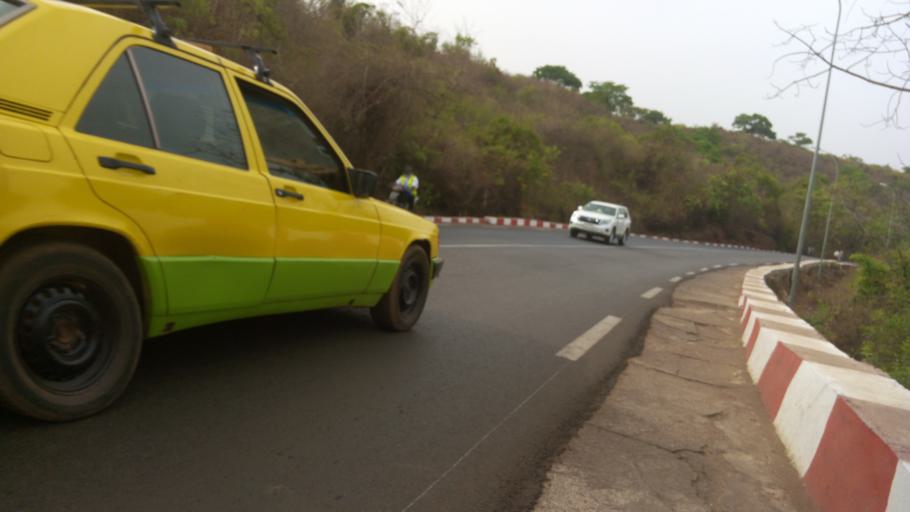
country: ML
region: Bamako
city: Bamako
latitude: 12.6697
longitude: -8.0063
